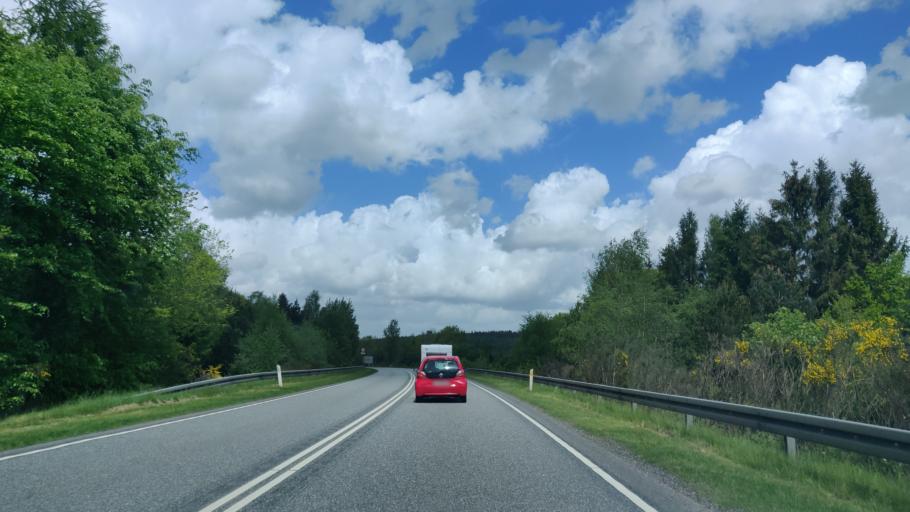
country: DK
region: Central Jutland
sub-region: Hedensted Kommune
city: Torring
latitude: 55.9639
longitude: 9.4057
